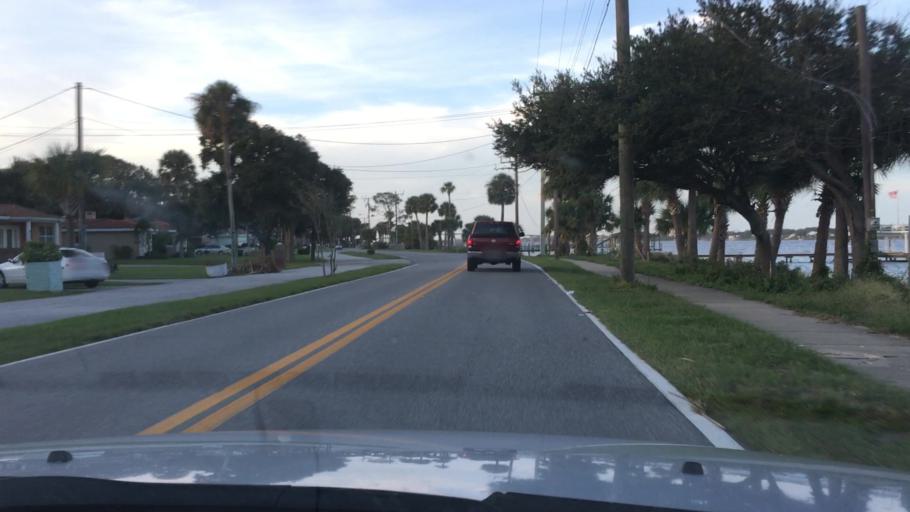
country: US
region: Florida
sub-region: Volusia County
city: Ormond Beach
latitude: 29.2698
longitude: -81.0473
